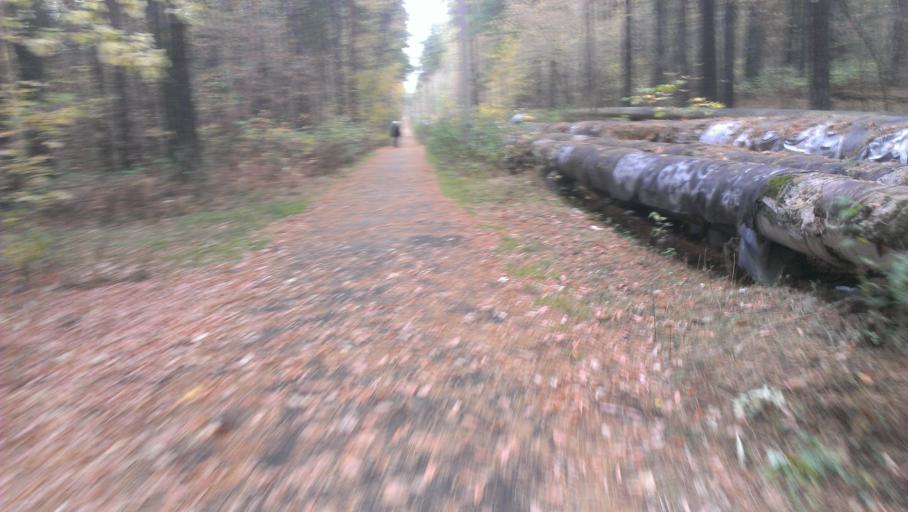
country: RU
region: Altai Krai
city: Yuzhnyy
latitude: 53.2591
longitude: 83.6894
